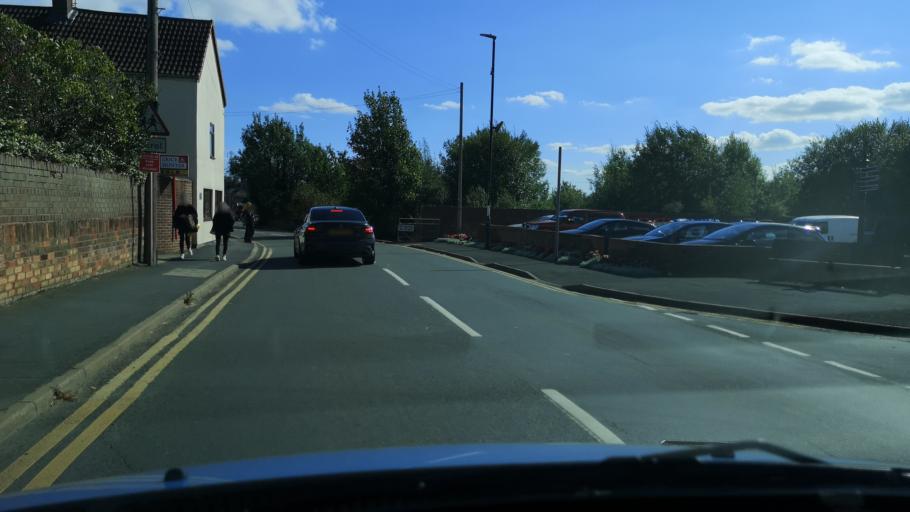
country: GB
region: England
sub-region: North Lincolnshire
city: Crowle
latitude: 53.6053
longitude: -0.8330
